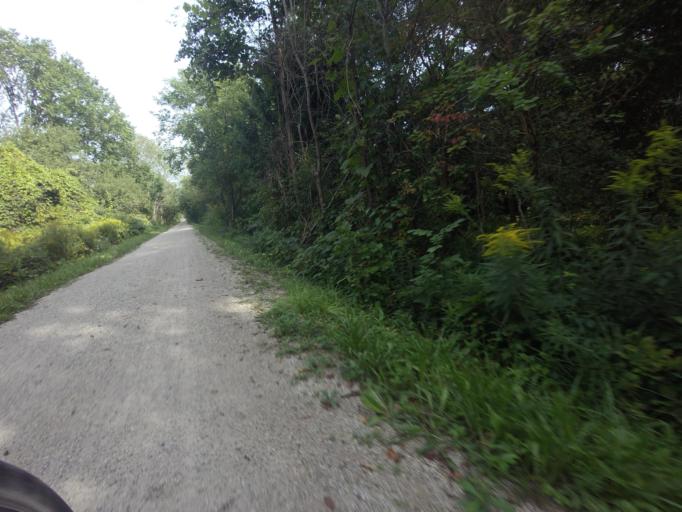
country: CA
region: Ontario
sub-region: Wellington County
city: Guelph
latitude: 43.5677
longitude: -80.3217
